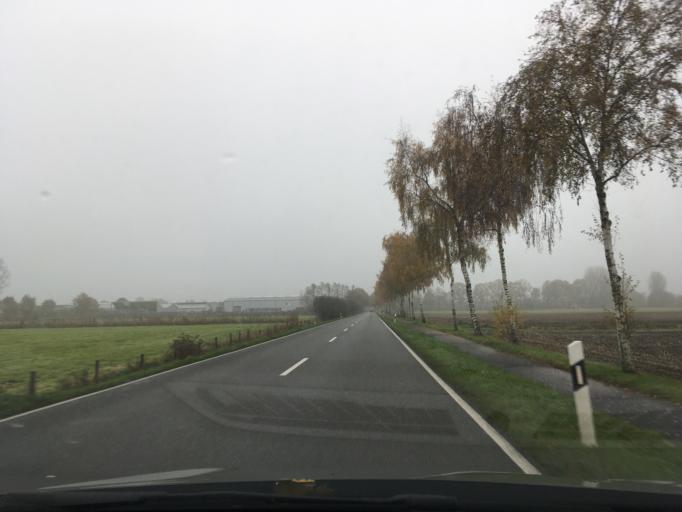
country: DE
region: North Rhine-Westphalia
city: Stadtlohn
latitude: 52.0838
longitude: 6.9153
